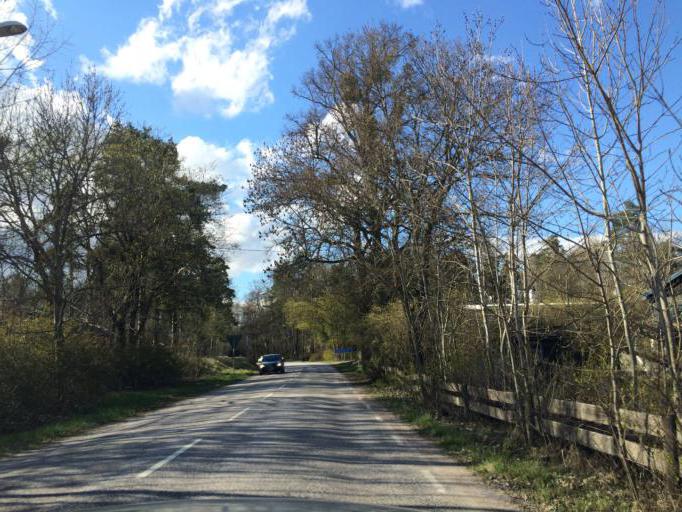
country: SE
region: Soedermanland
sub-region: Eskilstuna Kommun
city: Eskilstuna
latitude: 59.4122
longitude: 16.5822
